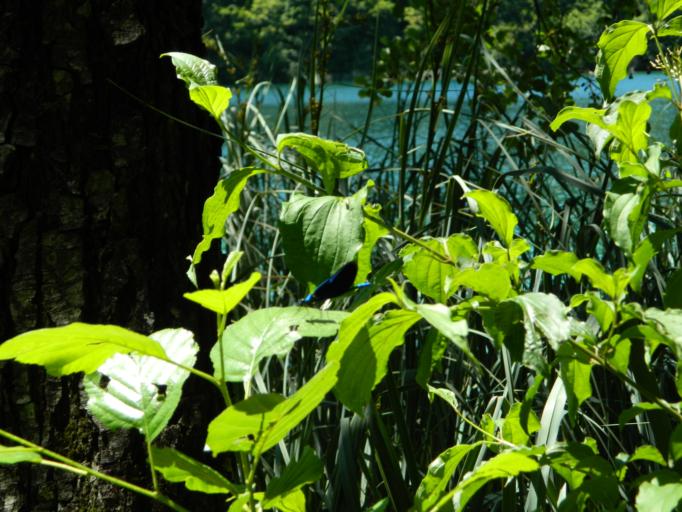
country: HR
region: Licko-Senjska
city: Jezerce
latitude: 44.8874
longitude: 15.6111
